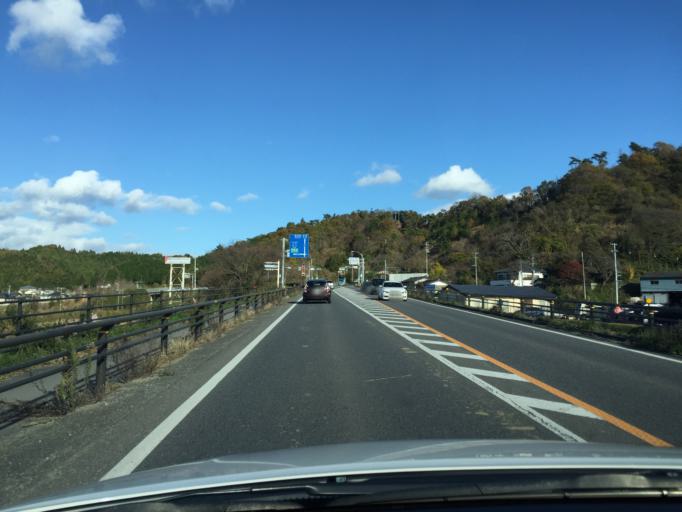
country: JP
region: Fukushima
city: Iwaki
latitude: 37.1483
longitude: 140.9956
